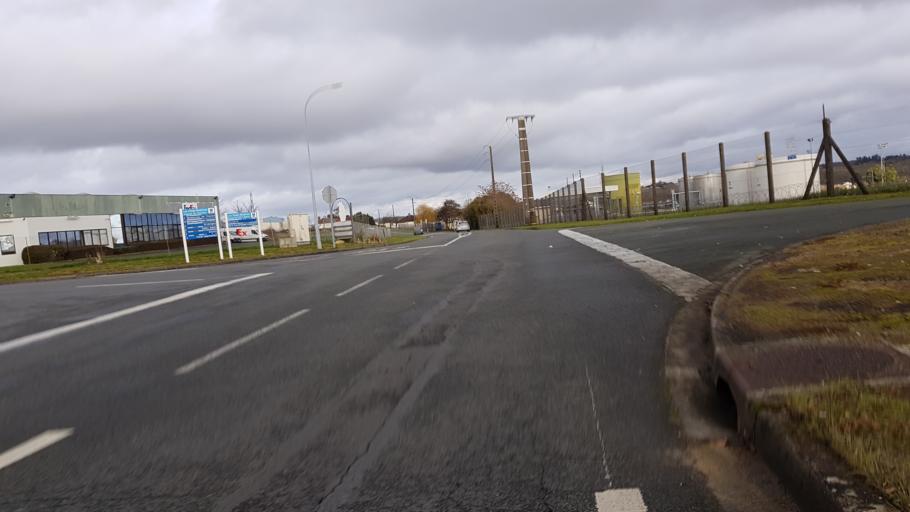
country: FR
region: Poitou-Charentes
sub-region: Departement de la Vienne
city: Chasseneuil-du-Poitou
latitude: 46.6553
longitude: 0.3727
